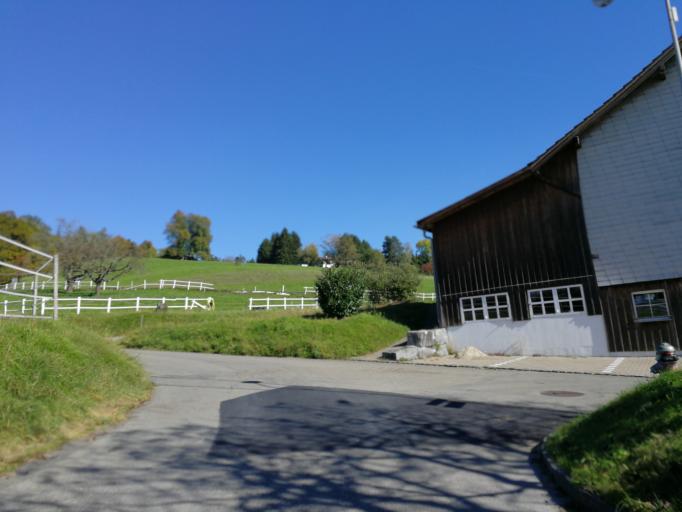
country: CH
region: Zurich
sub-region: Bezirk Meilen
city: Stafa
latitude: 47.2550
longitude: 8.7179
